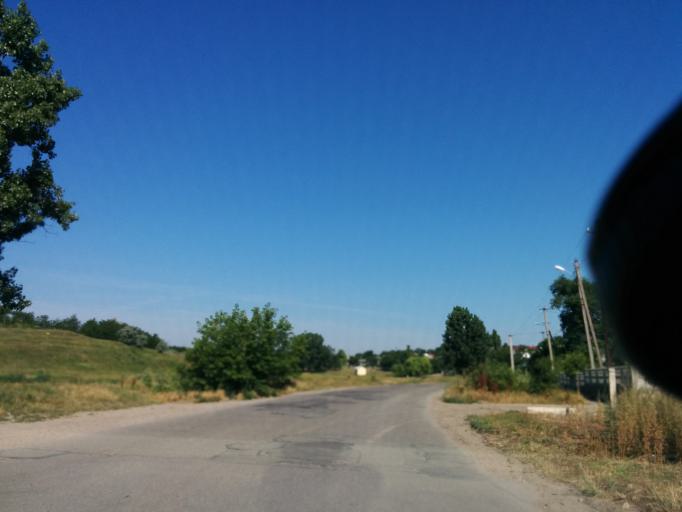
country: MD
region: Chisinau
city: Vadul lui Voda
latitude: 47.0632
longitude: 28.9973
